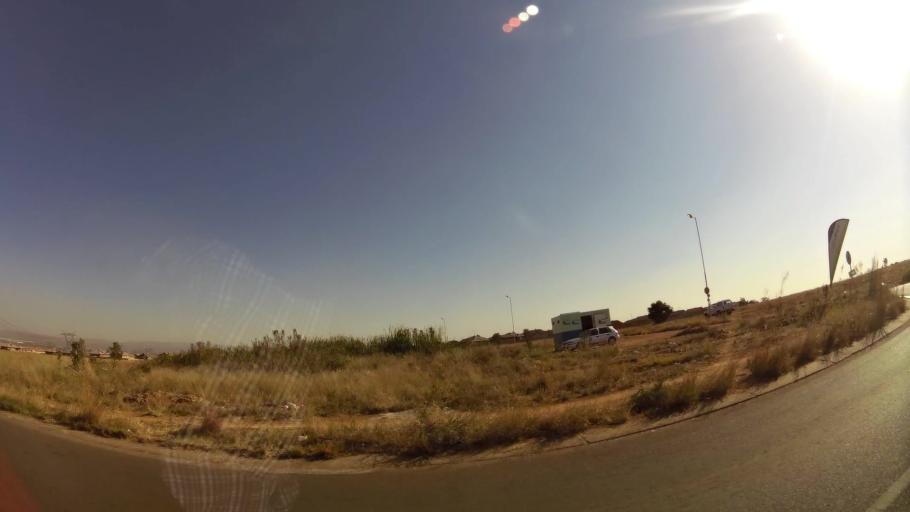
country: ZA
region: Gauteng
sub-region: City of Tshwane Metropolitan Municipality
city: Mabopane
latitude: -25.5602
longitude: 28.0970
